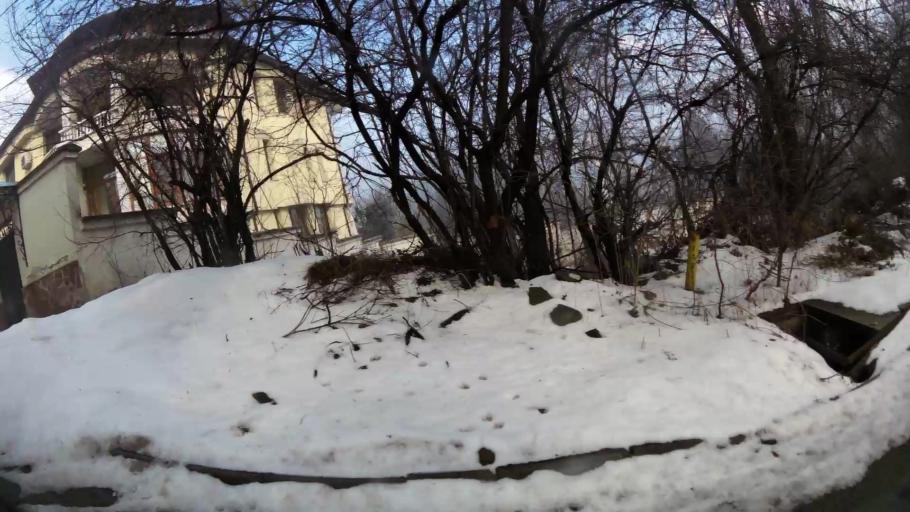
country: BG
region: Sofia-Capital
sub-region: Stolichna Obshtina
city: Sofia
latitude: 42.6509
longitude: 23.2612
